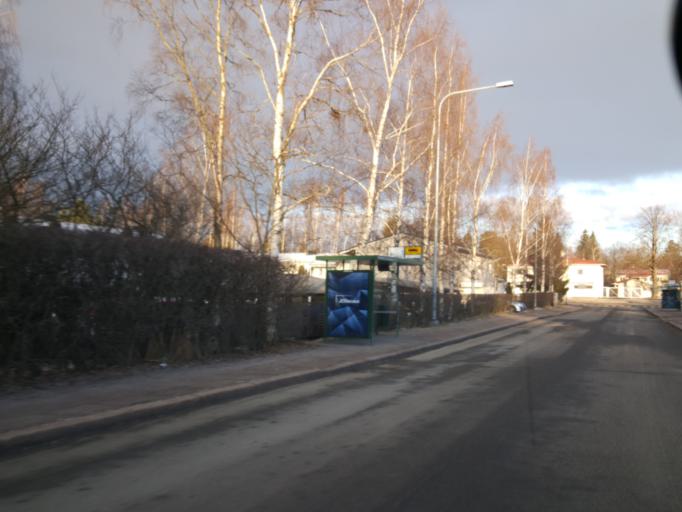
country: FI
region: Uusimaa
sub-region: Helsinki
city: Vantaa
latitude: 60.2505
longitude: 24.9869
